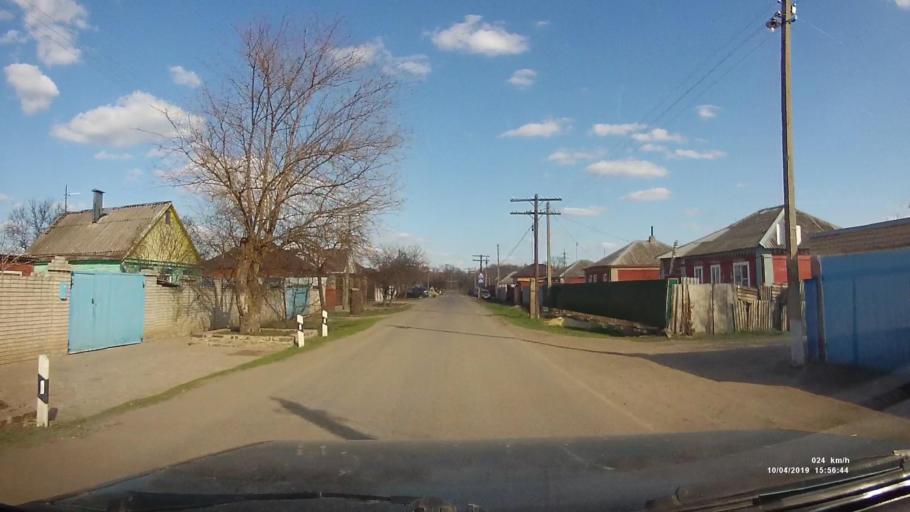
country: RU
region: Rostov
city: Masalovka
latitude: 48.4111
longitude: 40.2714
